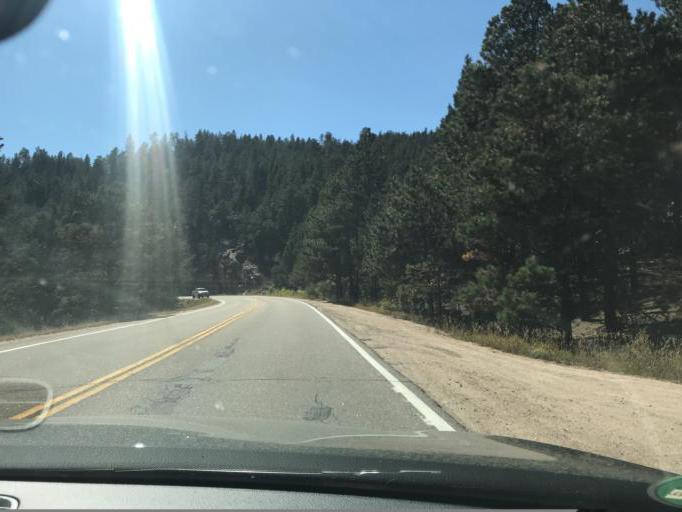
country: US
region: Colorado
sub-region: Boulder County
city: Nederland
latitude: 39.9762
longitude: -105.4629
